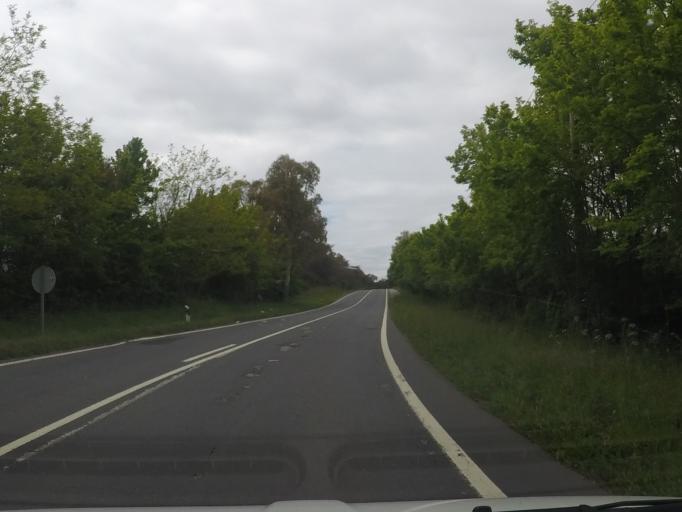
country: PT
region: Setubal
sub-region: Santiago do Cacem
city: Cercal
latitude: 37.8305
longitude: -8.7003
